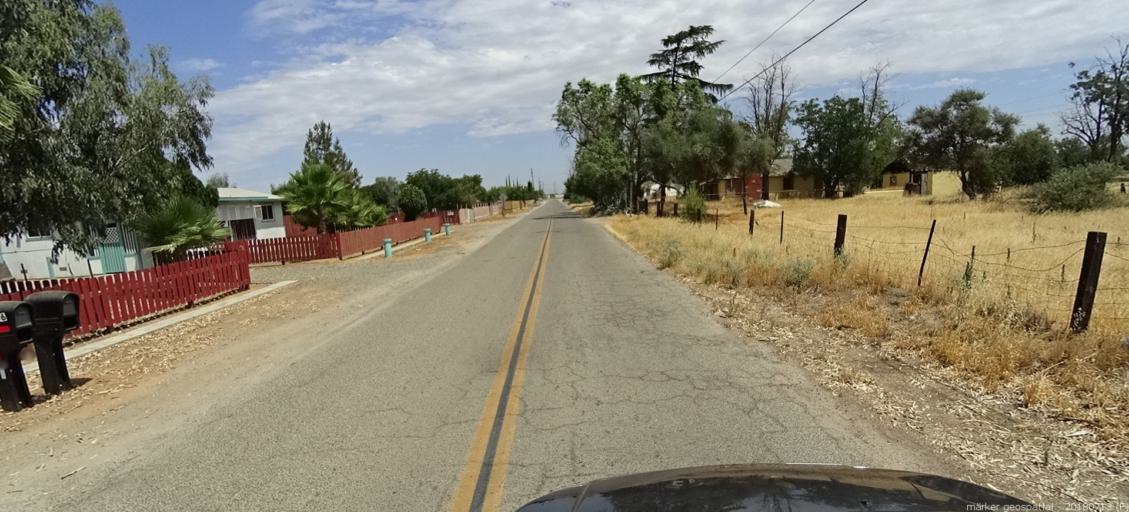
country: US
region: California
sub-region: Madera County
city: Madera
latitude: 36.9895
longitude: -120.0599
